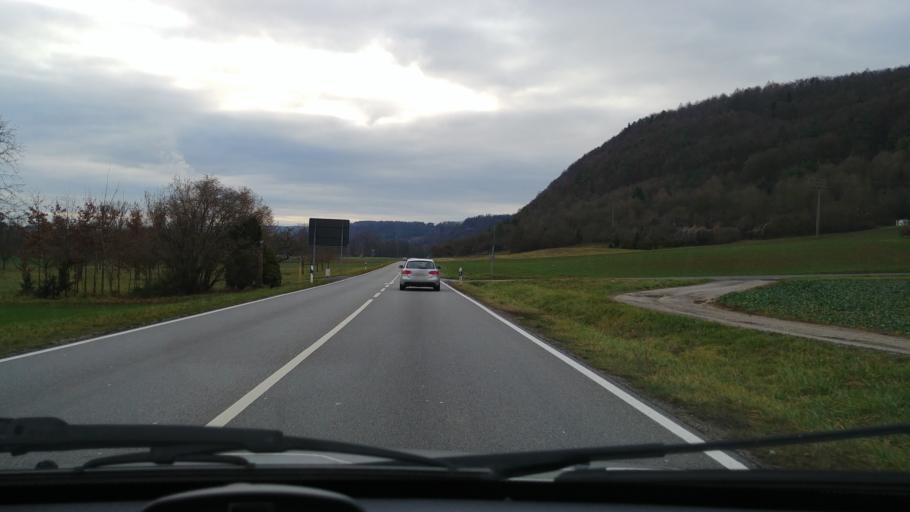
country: DE
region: Bavaria
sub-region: Regierungsbezirk Unterfranken
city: Karlstadt
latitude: 49.9722
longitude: 9.7588
